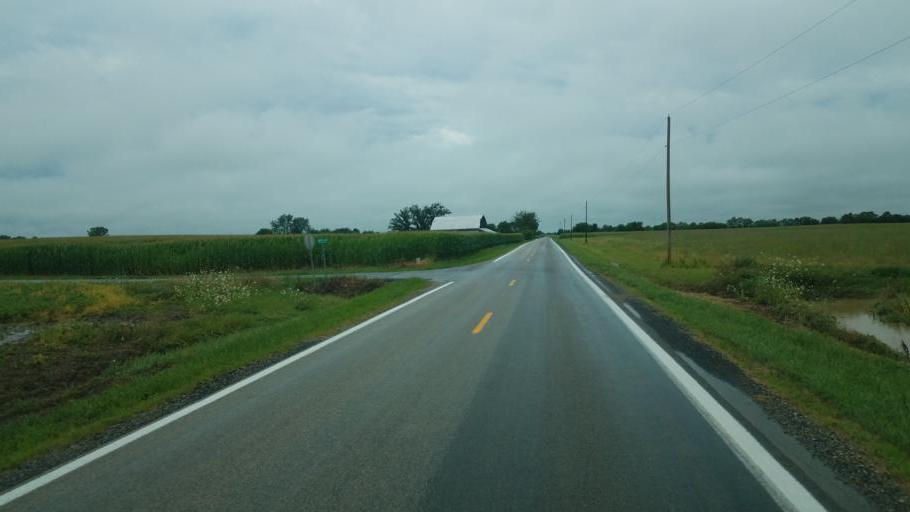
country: US
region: Ohio
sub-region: Union County
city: Richwood
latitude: 40.5271
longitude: -83.3501
